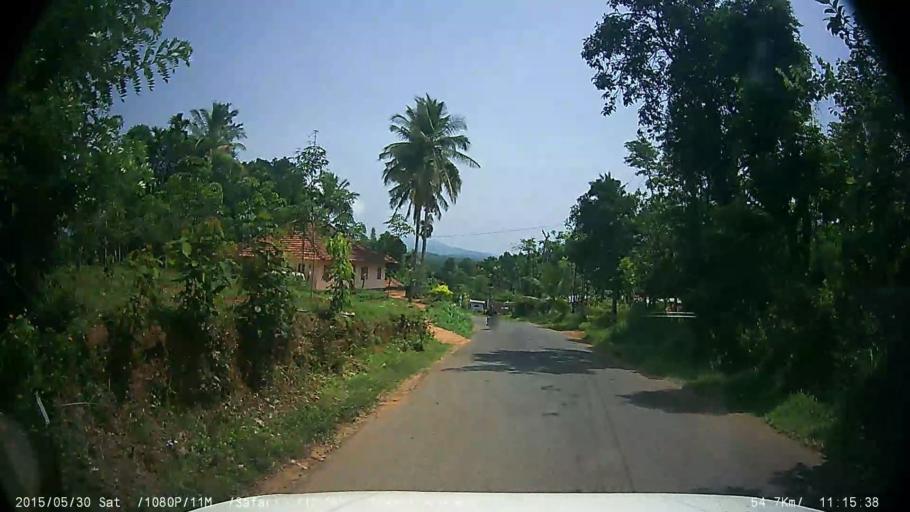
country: IN
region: Kerala
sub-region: Wayanad
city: Panamaram
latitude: 11.7719
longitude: 76.0600
